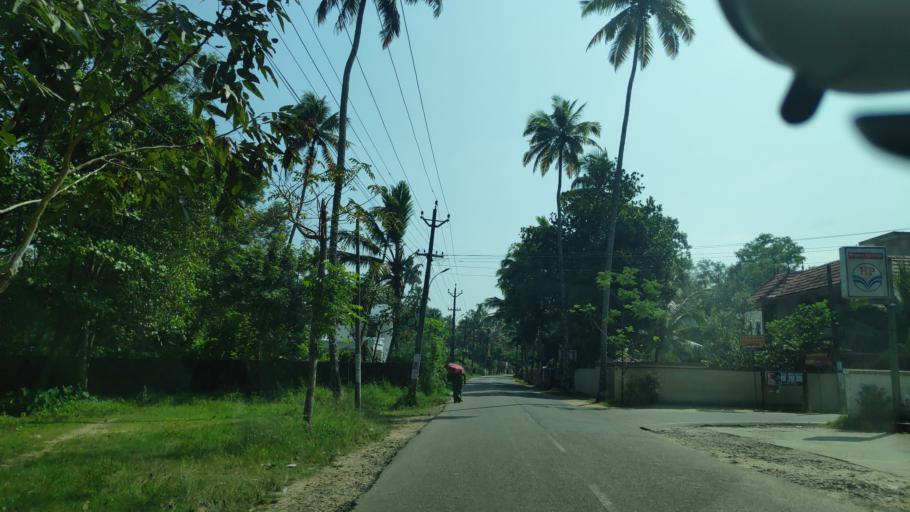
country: IN
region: Kerala
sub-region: Alappuzha
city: Vayalar
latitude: 9.6417
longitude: 76.2985
